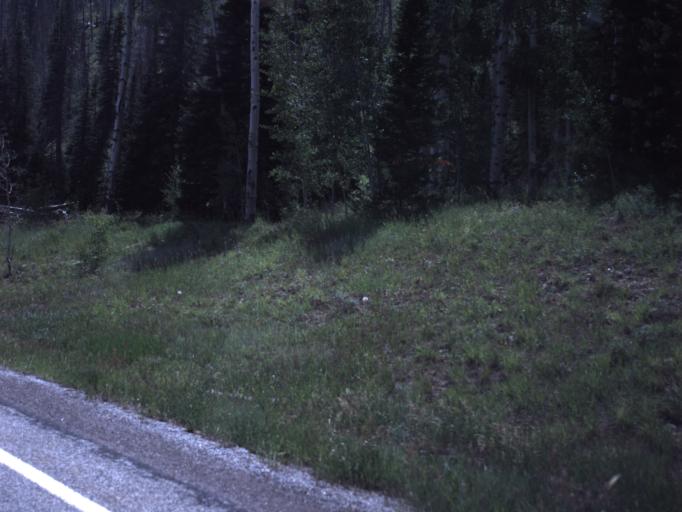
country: US
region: Utah
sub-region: Sanpete County
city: Fairview
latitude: 39.5477
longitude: -111.1673
